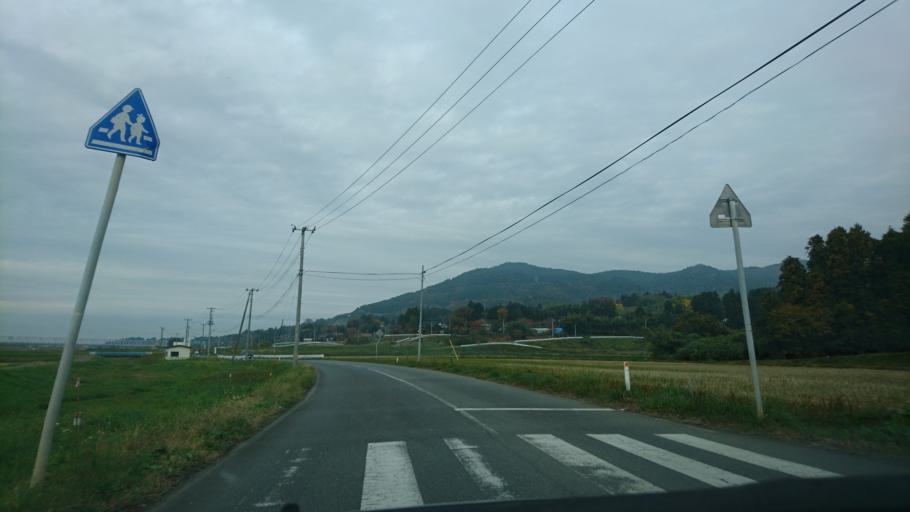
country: JP
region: Iwate
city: Ichinoseki
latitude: 38.9663
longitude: 141.1668
